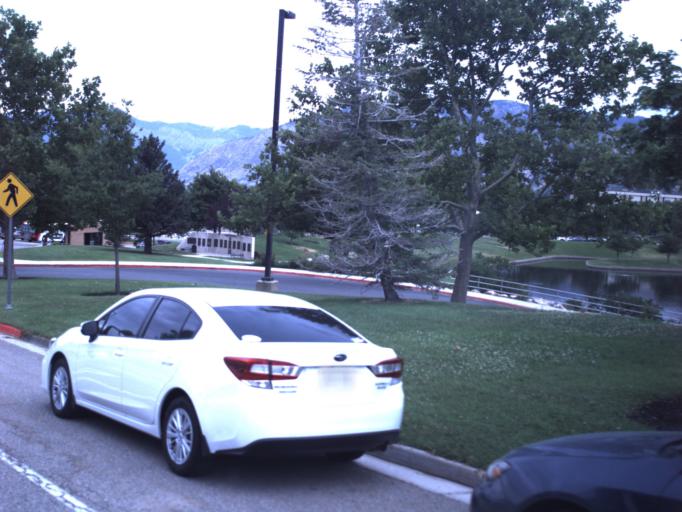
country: US
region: Utah
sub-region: Weber County
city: South Ogden
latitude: 41.1913
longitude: -111.9481
